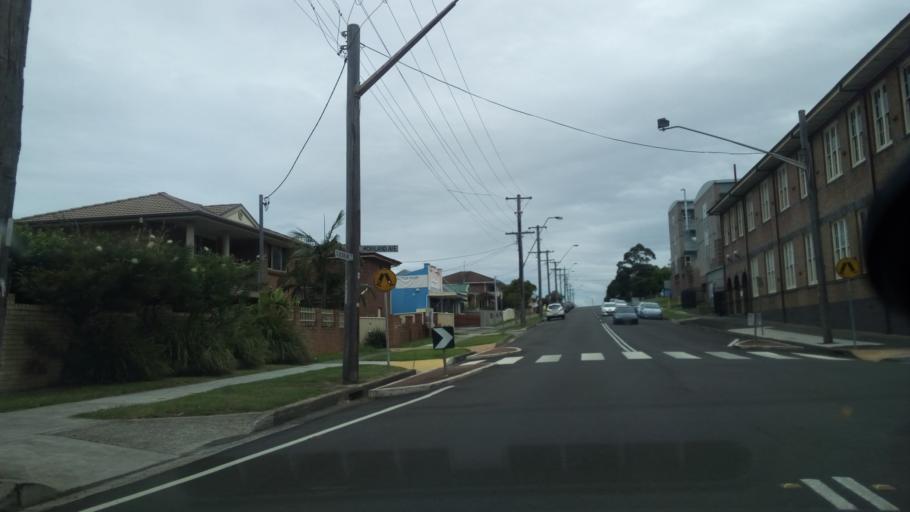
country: AU
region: New South Wales
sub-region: Wollongong
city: Wollongong
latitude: -34.4286
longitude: 150.8868
